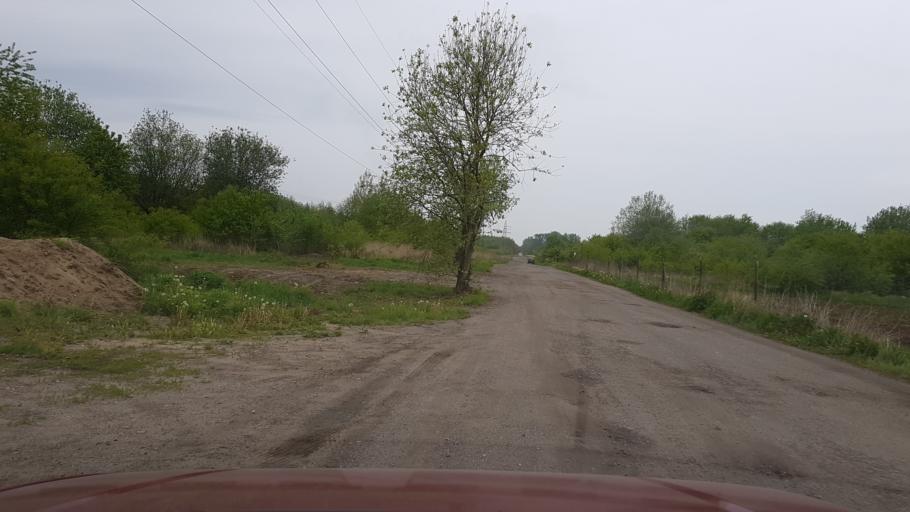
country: PL
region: West Pomeranian Voivodeship
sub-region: Koszalin
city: Koszalin
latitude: 54.1702
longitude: 16.1908
